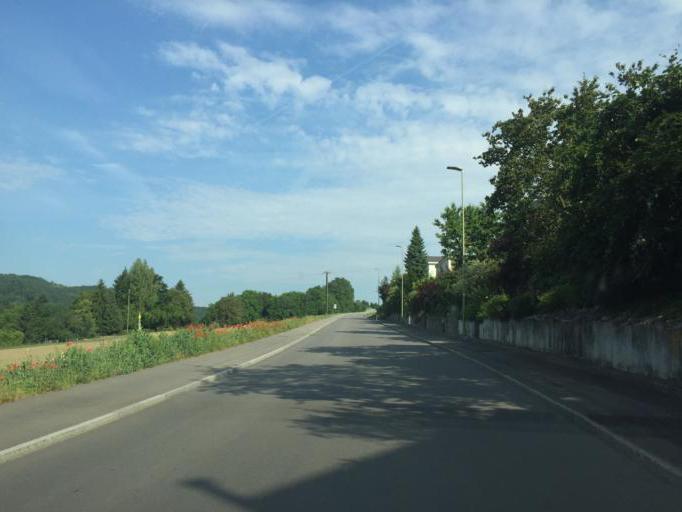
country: CH
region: Zurich
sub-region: Bezirk Buelach
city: Freienstein
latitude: 47.5366
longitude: 8.5797
